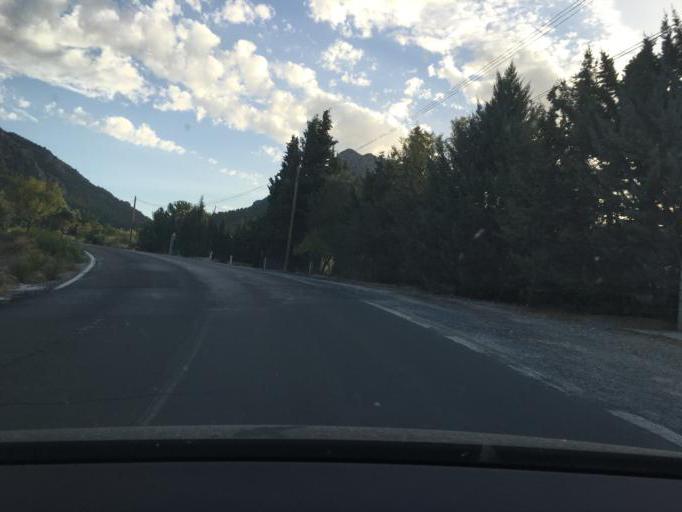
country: ES
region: Andalusia
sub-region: Provincia de Granada
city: Huetor Santillan
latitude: 37.2313
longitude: -3.4979
